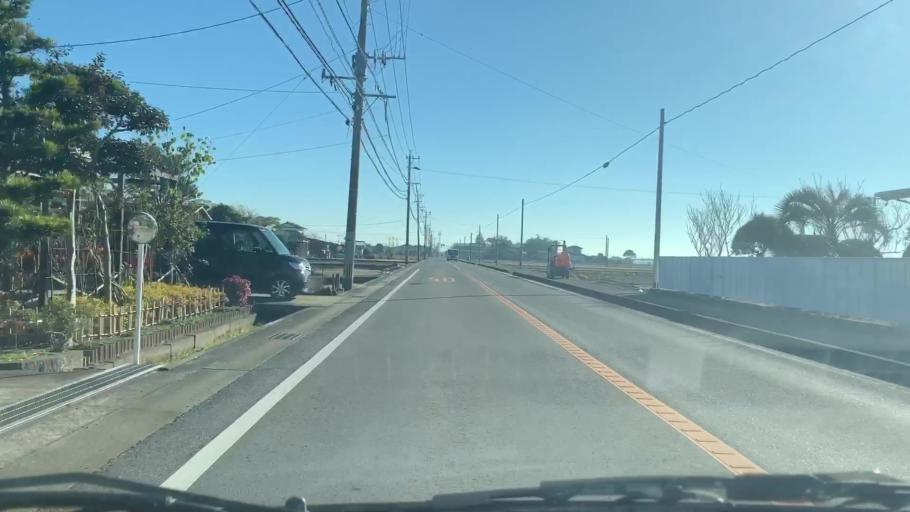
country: JP
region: Saga Prefecture
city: Kashima
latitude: 33.1840
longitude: 130.1666
